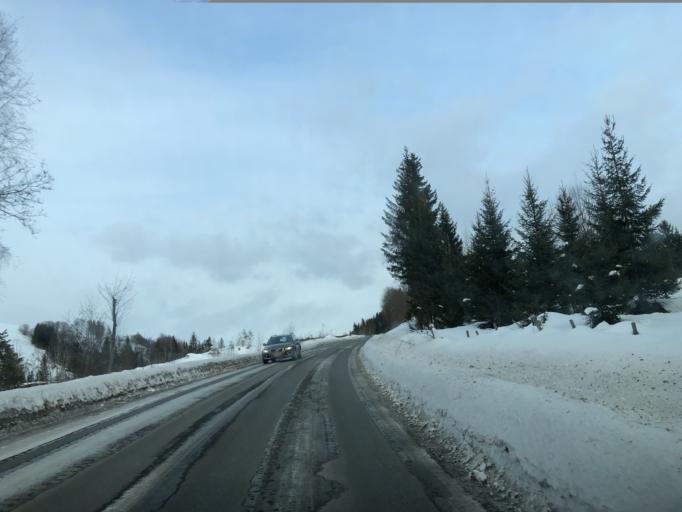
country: NO
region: Oppland
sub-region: Gausdal
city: Segalstad bru
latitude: 61.2775
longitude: 10.1493
